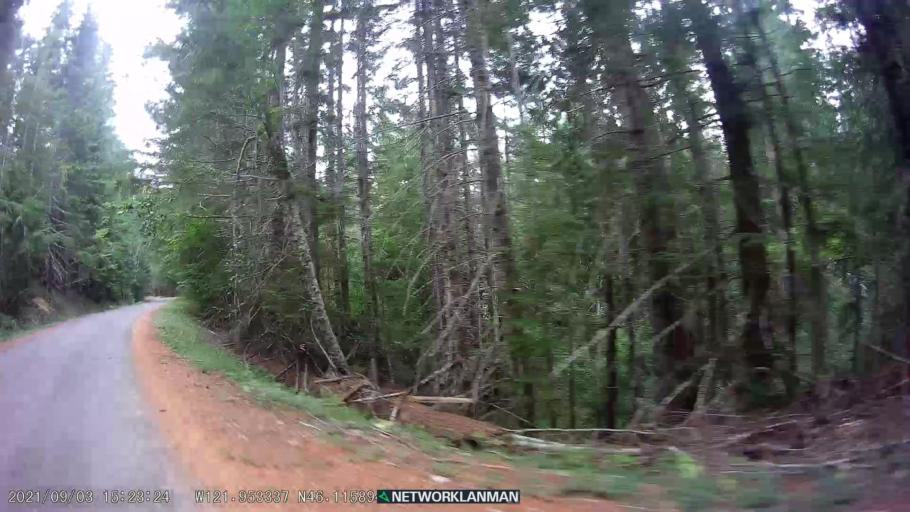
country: US
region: Washington
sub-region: Skamania County
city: Carson
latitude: 46.1158
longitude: -121.9531
